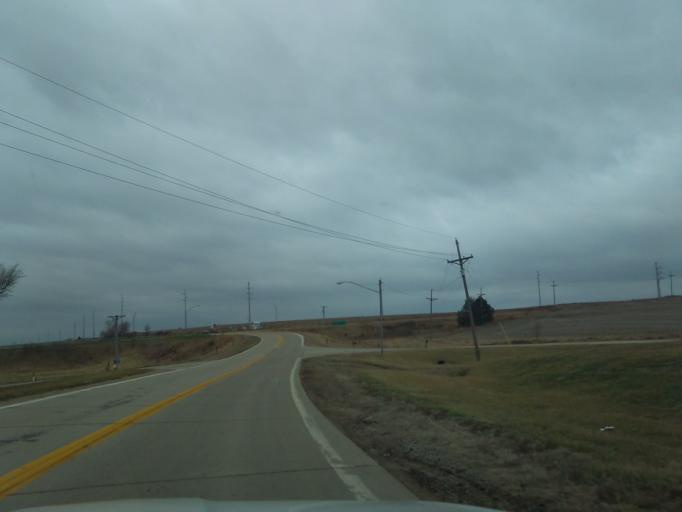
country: US
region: Nebraska
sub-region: Nemaha County
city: Auburn
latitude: 40.4672
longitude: -95.7339
